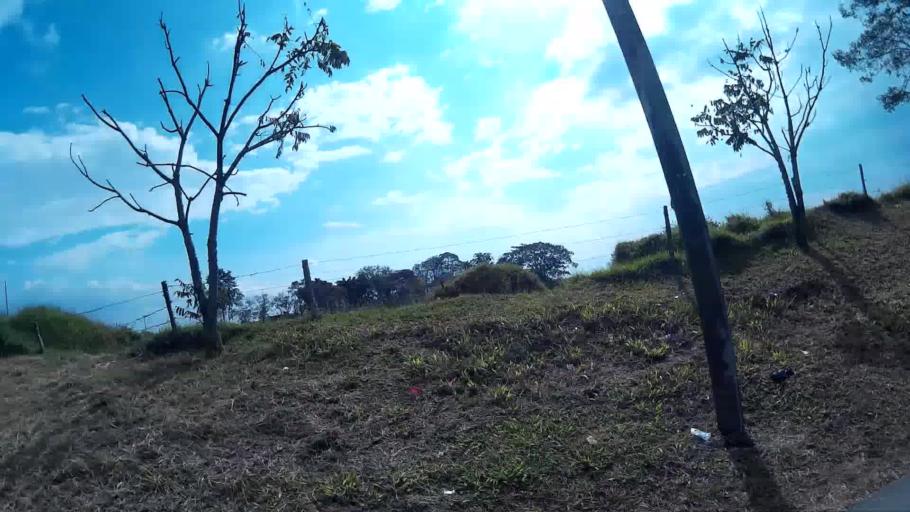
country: CO
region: Quindio
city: Filandia
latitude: 4.6895
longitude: -75.6073
